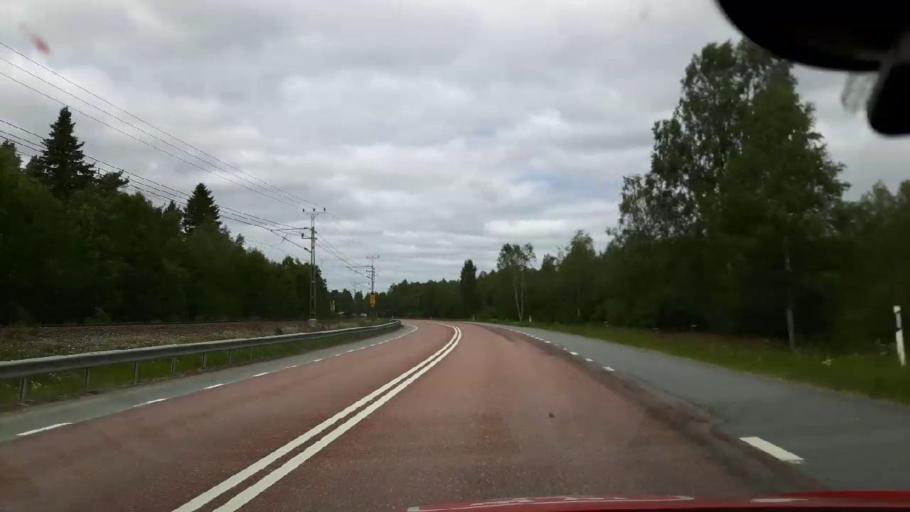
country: SE
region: Jaemtland
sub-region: Braecke Kommun
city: Braecke
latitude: 62.9135
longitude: 15.2606
